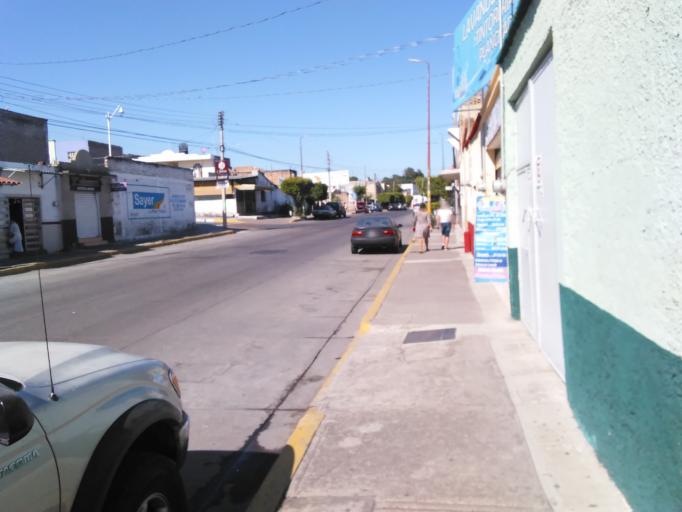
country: MX
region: Nayarit
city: Tepic
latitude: 21.5130
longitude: -104.8867
